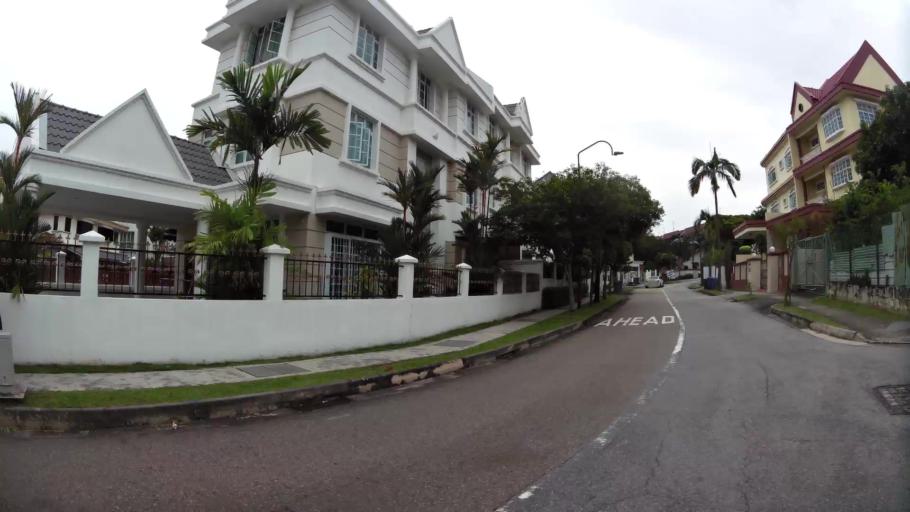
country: SG
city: Singapore
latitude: 1.3606
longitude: 103.8809
